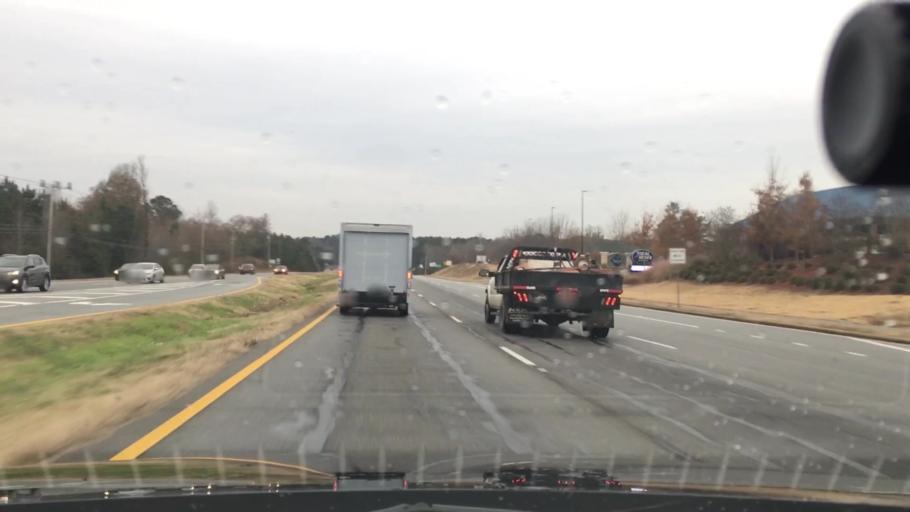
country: US
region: Georgia
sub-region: Fayette County
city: Peachtree City
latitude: 33.3983
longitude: -84.6233
